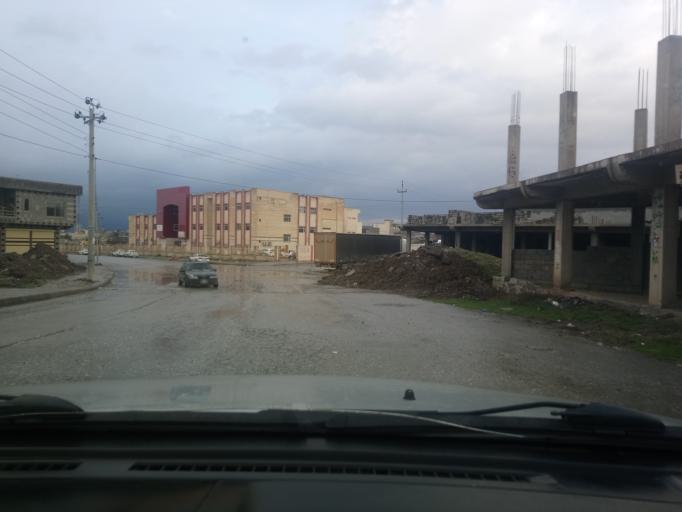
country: IQ
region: As Sulaymaniyah
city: Qeladize
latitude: 36.1810
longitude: 45.1375
